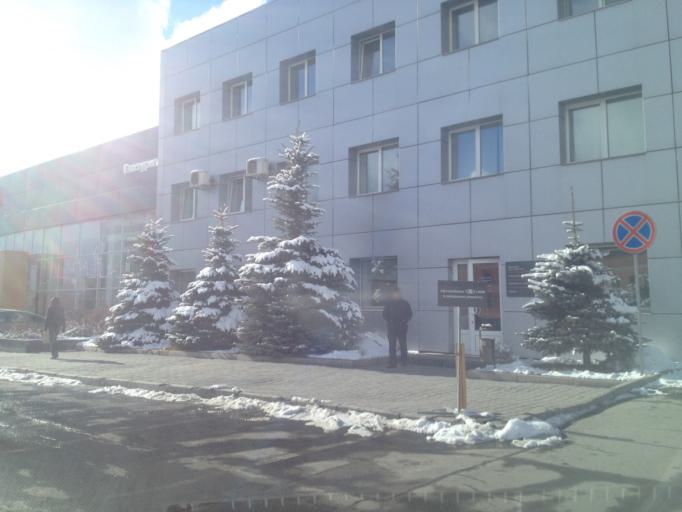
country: RU
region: Sverdlovsk
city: Yekaterinburg
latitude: 56.8841
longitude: 60.6404
